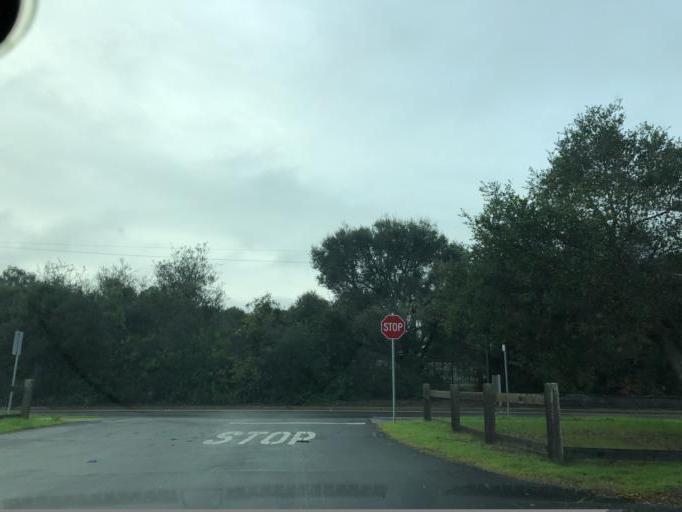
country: US
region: California
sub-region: Santa Clara County
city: Stanford
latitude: 37.4299
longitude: -122.1810
